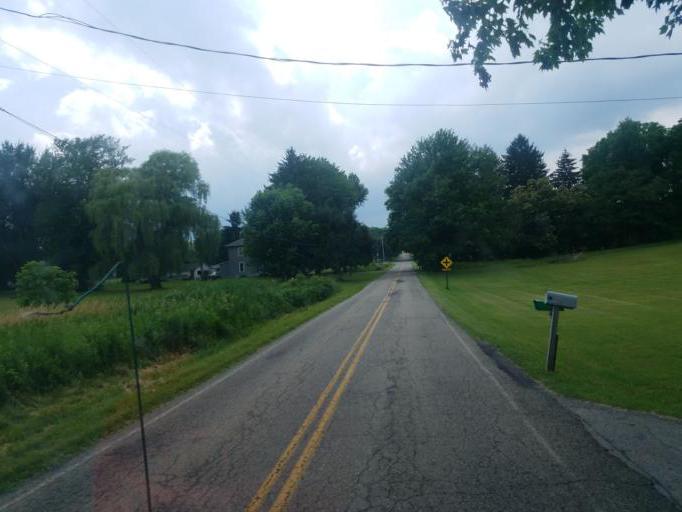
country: US
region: Ohio
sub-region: Columbiana County
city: Salem
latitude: 40.9739
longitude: -80.9030
